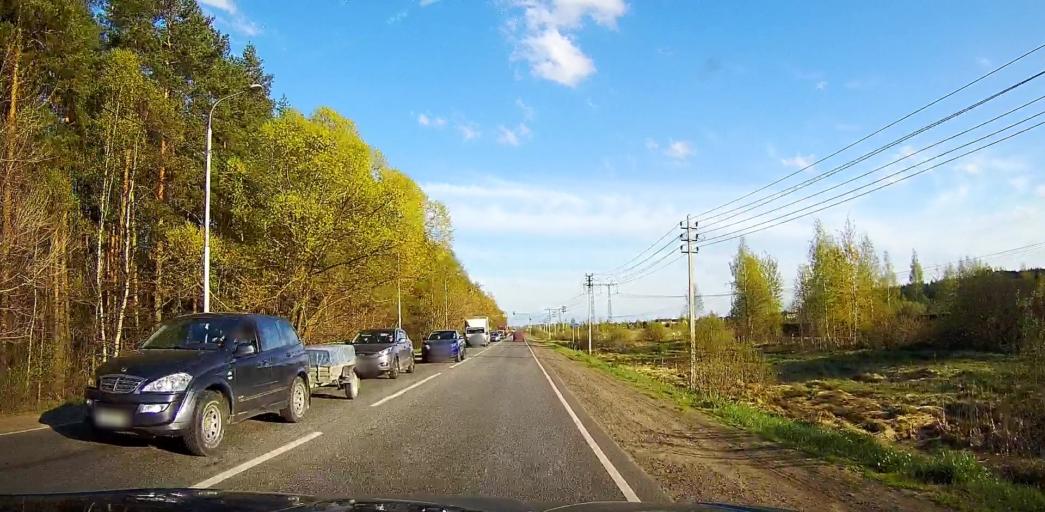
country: RU
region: Moskovskaya
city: Bronnitsy
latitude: 55.3787
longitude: 38.2098
